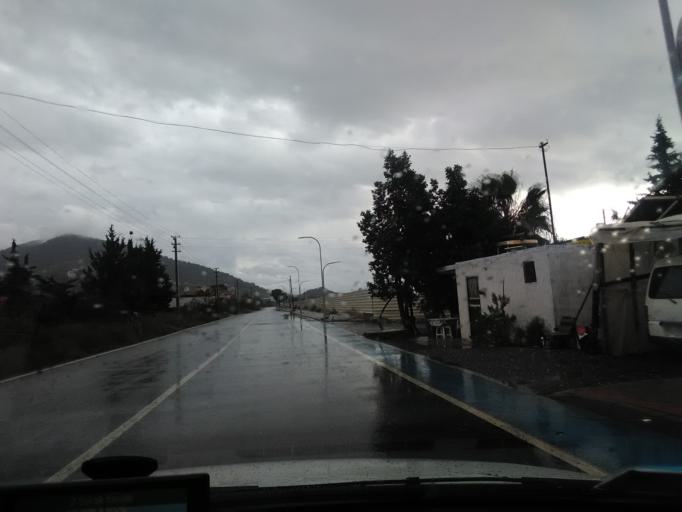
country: TR
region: Antalya
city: Gazipasa
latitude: 36.2536
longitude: 32.2913
